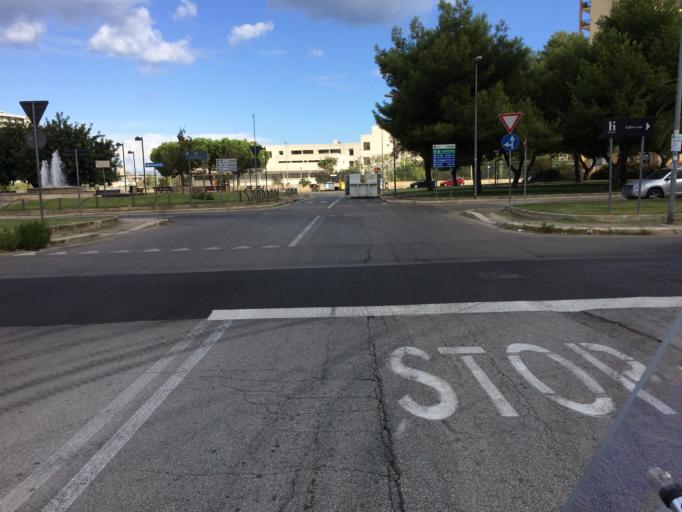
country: IT
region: Apulia
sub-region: Provincia di Bari
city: Bari
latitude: 41.0957
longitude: 16.8576
